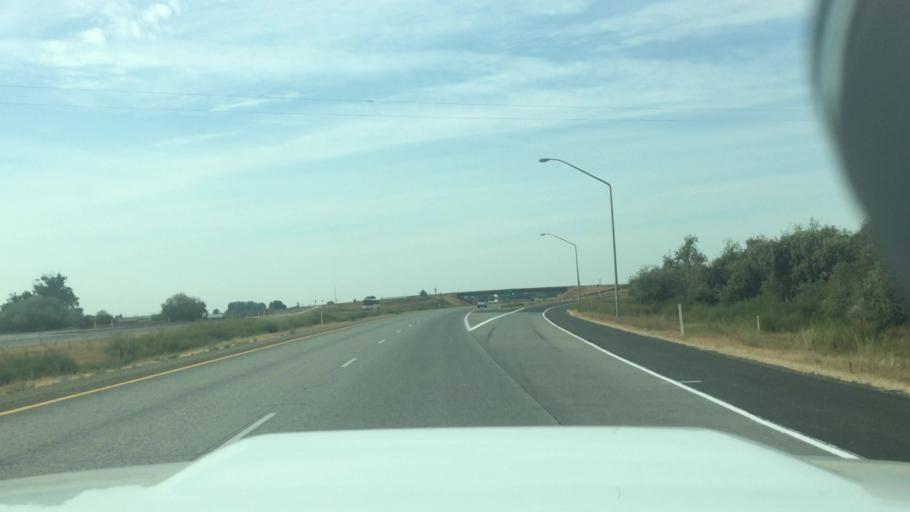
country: US
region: Washington
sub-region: Yakima County
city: Sunnyside
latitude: 46.3239
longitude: -120.0724
